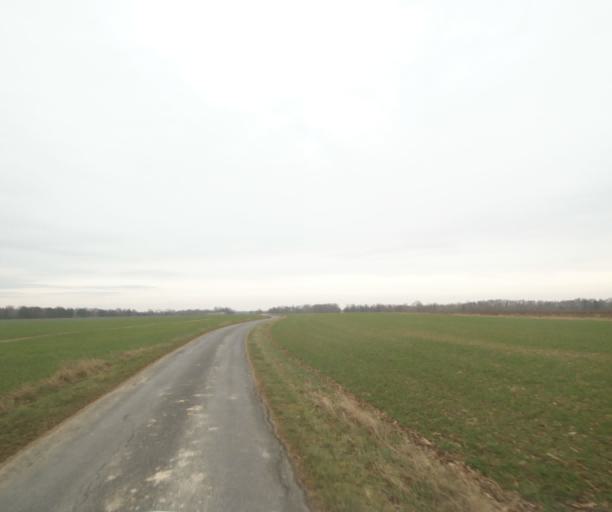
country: FR
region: Champagne-Ardenne
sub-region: Departement de la Haute-Marne
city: Villiers-en-Lieu
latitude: 48.6374
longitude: 4.7993
